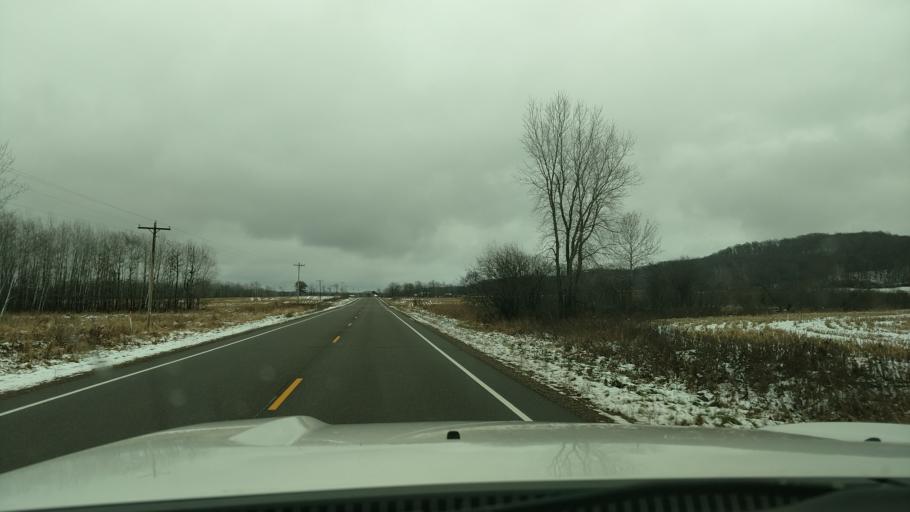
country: US
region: Wisconsin
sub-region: Dunn County
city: Colfax
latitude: 45.1382
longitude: -91.7804
